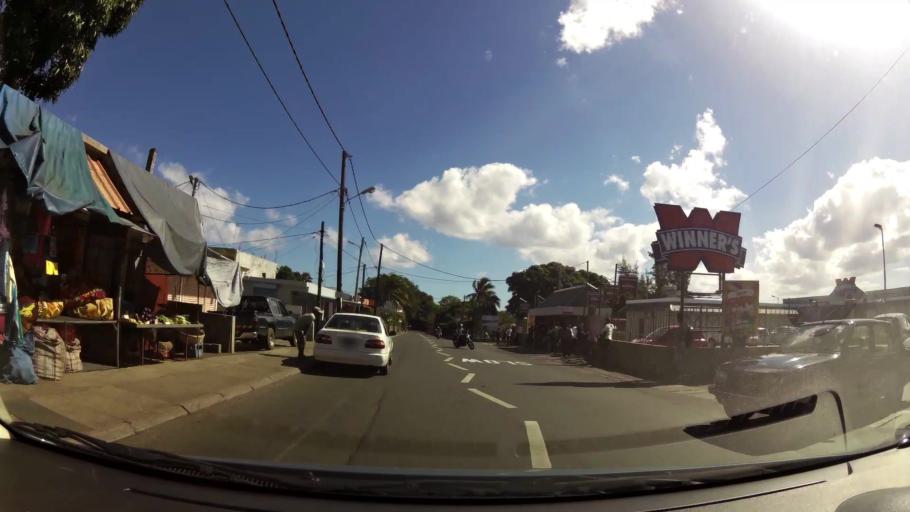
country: MU
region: Black River
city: Cascavelle
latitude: -20.2571
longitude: 57.4127
